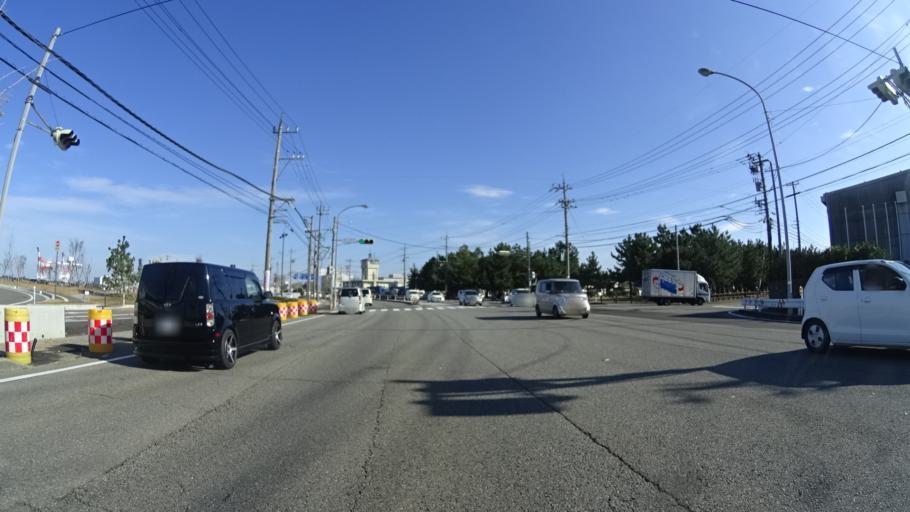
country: JP
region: Ishikawa
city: Kanazawa-shi
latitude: 36.6071
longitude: 136.6145
